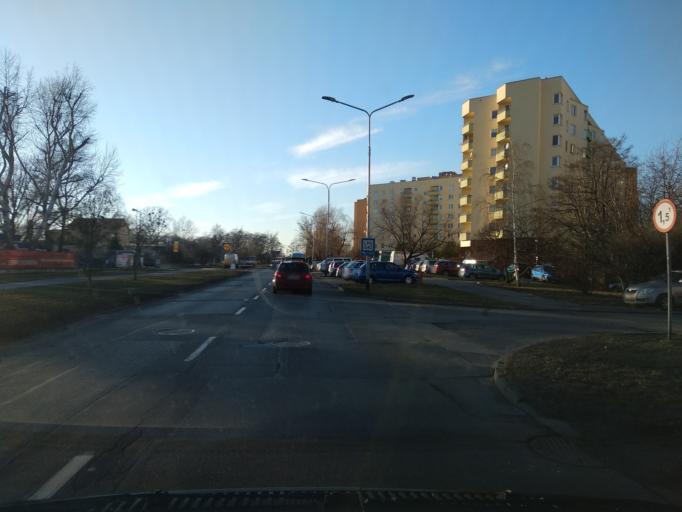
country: PL
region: Lower Silesian Voivodeship
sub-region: Powiat wroclawski
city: Wroclaw
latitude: 51.1221
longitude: 16.9647
